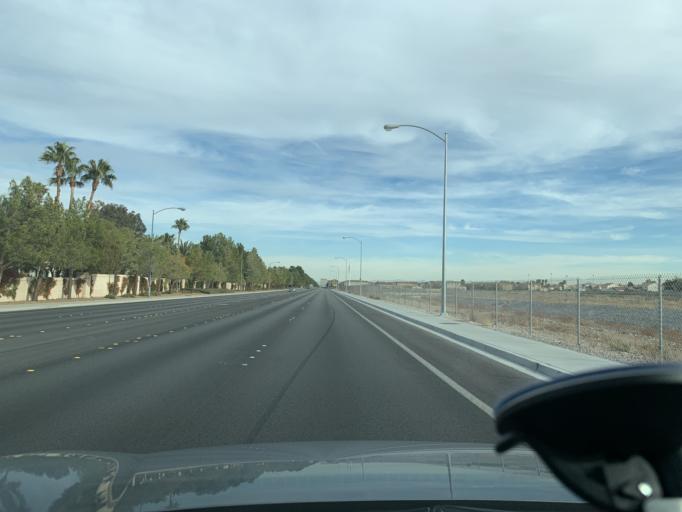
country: US
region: Nevada
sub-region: Clark County
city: Spring Valley
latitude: 36.0922
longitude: -115.2564
